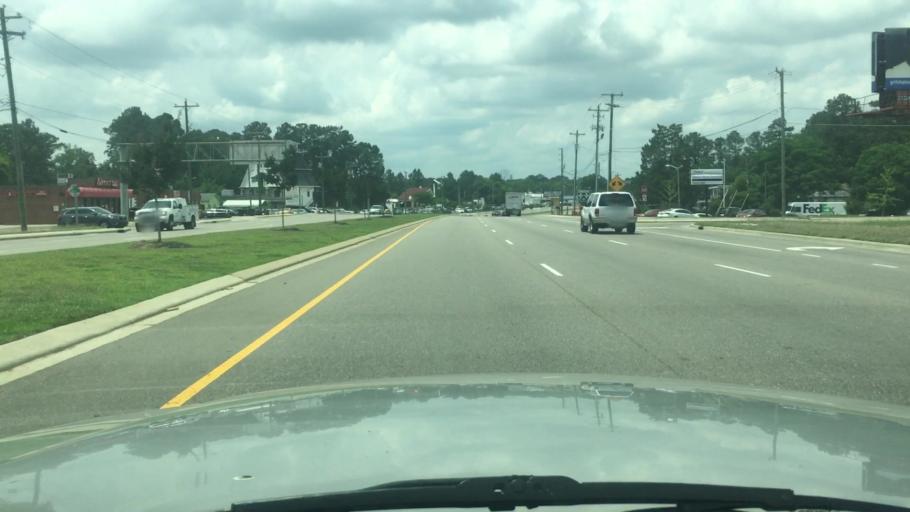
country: US
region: North Carolina
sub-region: Cumberland County
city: Fort Bragg
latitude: 35.0869
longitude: -78.9512
